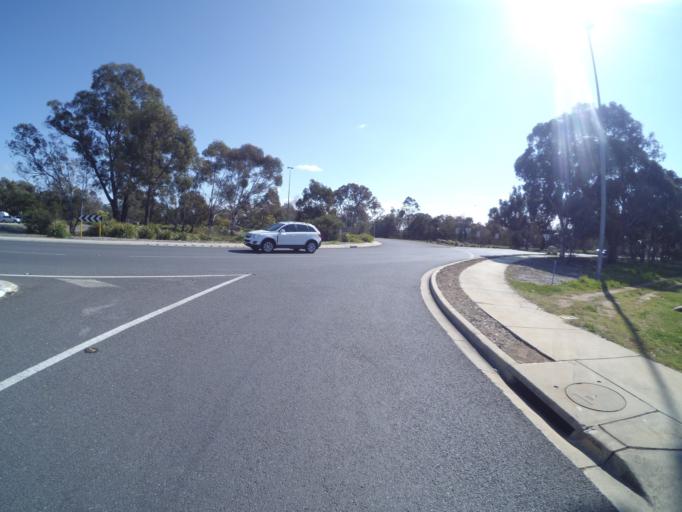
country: AU
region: Australian Capital Territory
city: Kaleen
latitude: -35.2253
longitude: 149.1654
